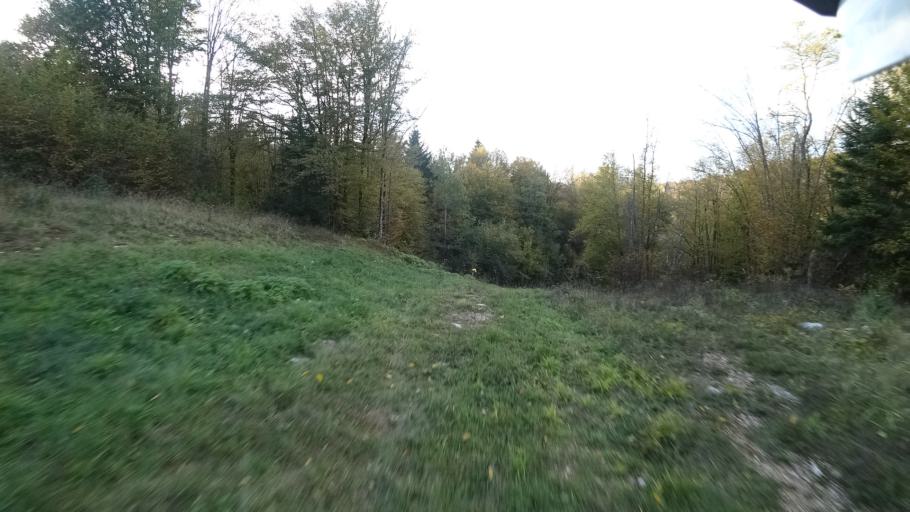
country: HR
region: Karlovacka
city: Plaski
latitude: 45.0087
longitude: 15.4221
